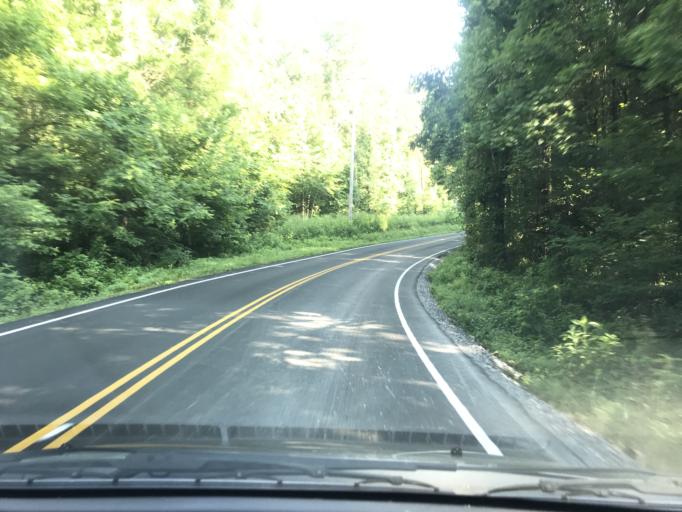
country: US
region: Tennessee
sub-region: Loudon County
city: Loudon
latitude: 35.7934
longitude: -84.3630
